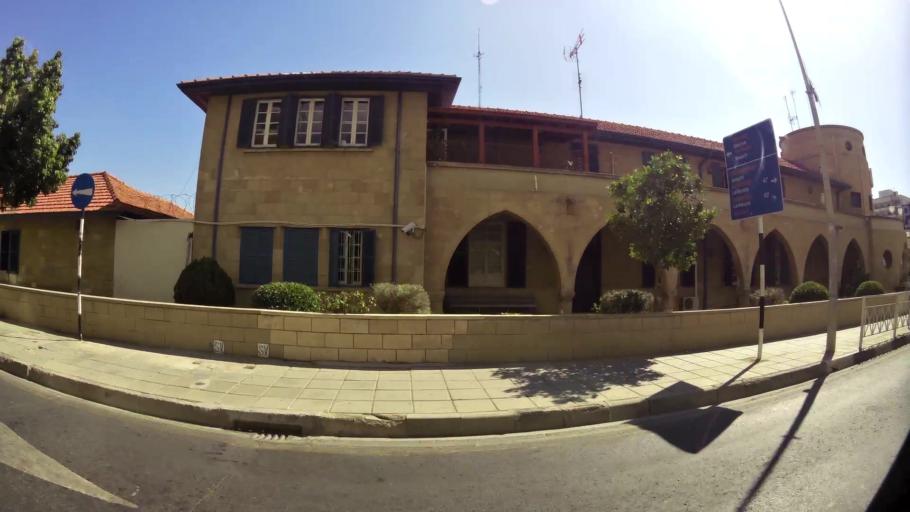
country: CY
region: Larnaka
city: Larnaca
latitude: 34.9181
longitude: 33.6366
